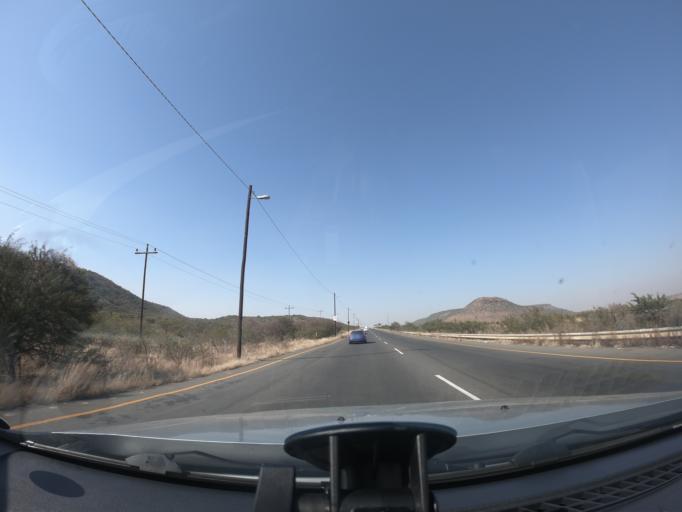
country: ZA
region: KwaZulu-Natal
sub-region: uThukela District Municipality
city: Ladysmith
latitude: -28.5552
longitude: 29.8367
